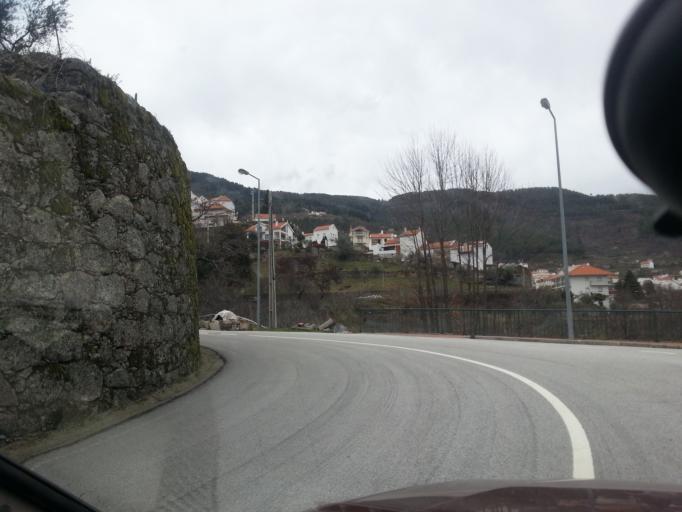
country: PT
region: Guarda
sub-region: Manteigas
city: Manteigas
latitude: 40.3965
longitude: -7.5417
